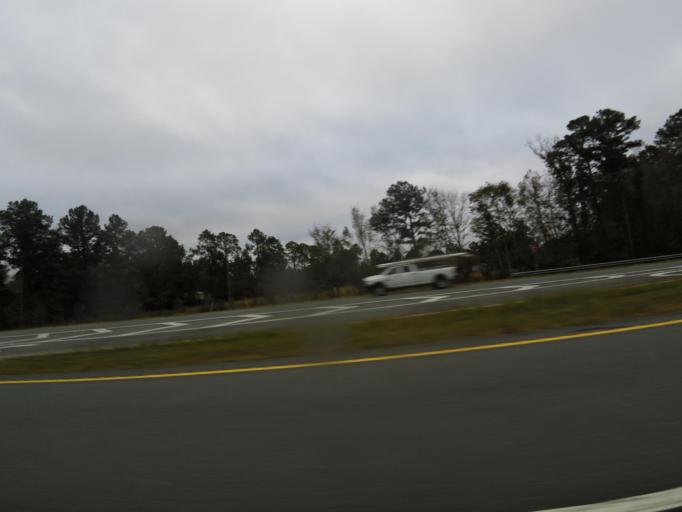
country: US
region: Georgia
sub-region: Charlton County
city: Folkston
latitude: 30.9085
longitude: -82.0730
